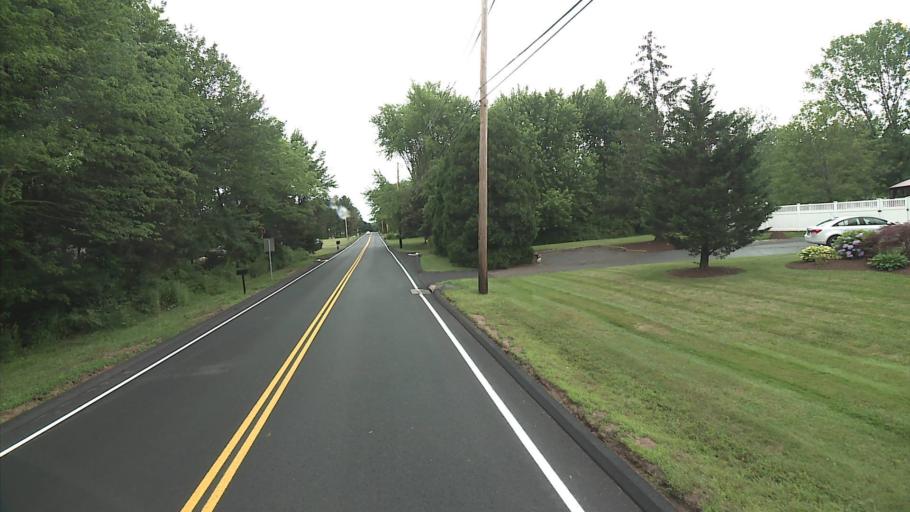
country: US
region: Connecticut
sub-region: New Haven County
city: Wallingford Center
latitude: 41.3966
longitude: -72.7966
